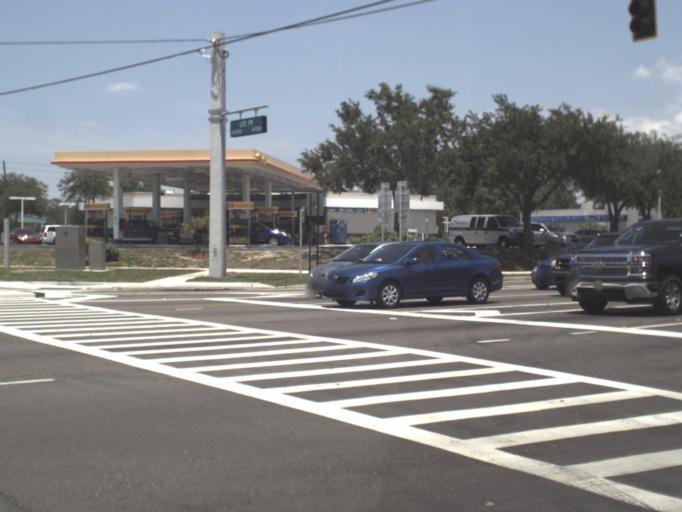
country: US
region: Florida
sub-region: Pinellas County
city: Tarpon Springs
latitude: 28.1461
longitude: -82.7402
